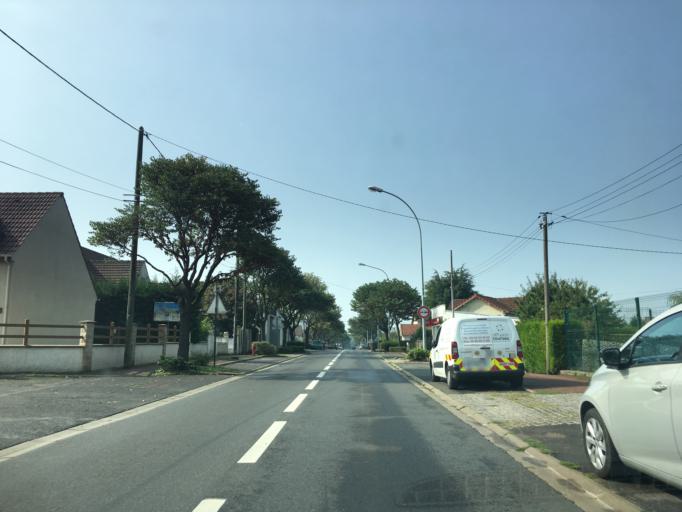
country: FR
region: Ile-de-France
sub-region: Departement du Val-de-Marne
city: Noiseau
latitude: 48.7744
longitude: 2.5467
